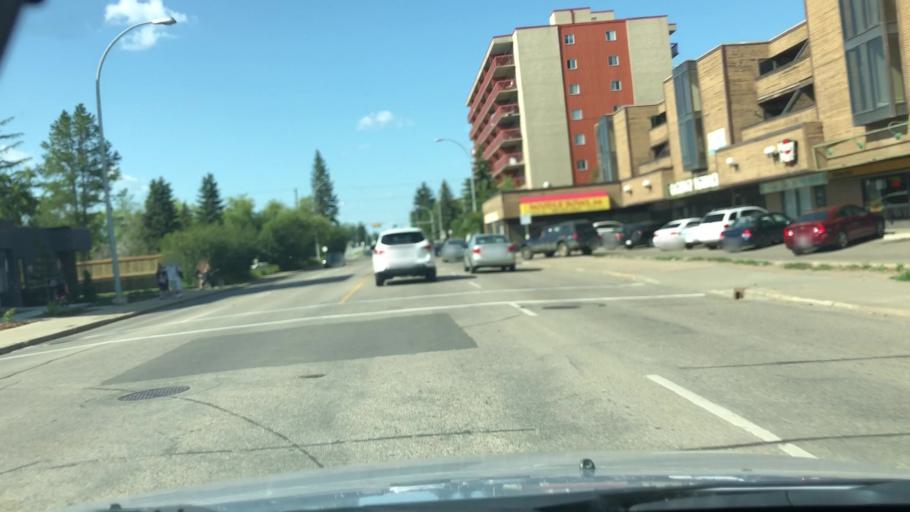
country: CA
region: Alberta
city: Edmonton
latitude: 53.5859
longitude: -113.4429
